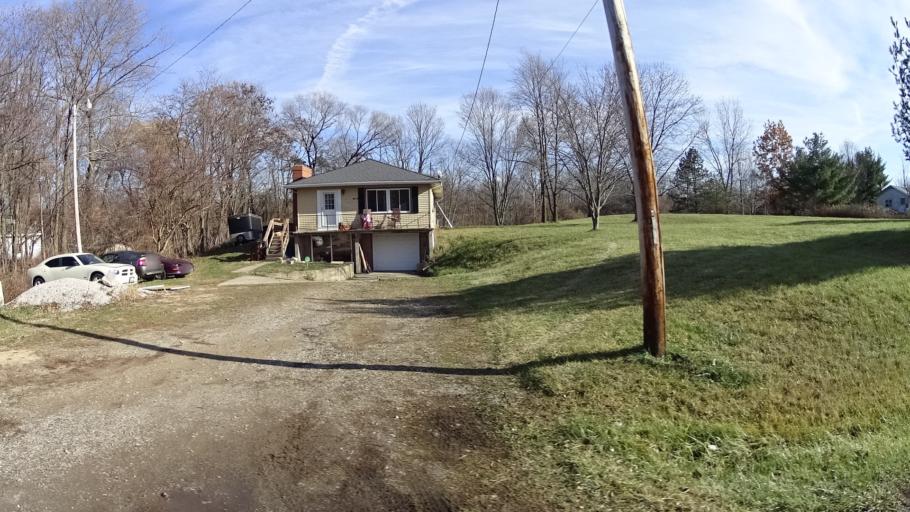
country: US
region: Ohio
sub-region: Lorain County
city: Wellington
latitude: 41.0735
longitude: -82.2593
